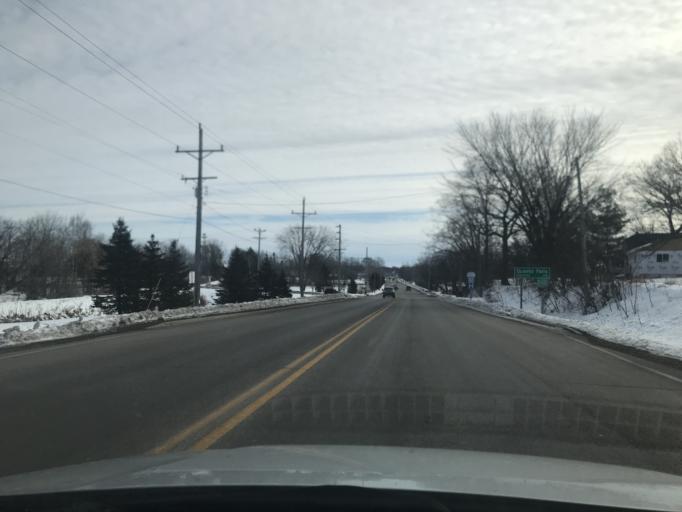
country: US
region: Wisconsin
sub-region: Oconto County
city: Oconto Falls
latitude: 44.8833
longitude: -88.1531
